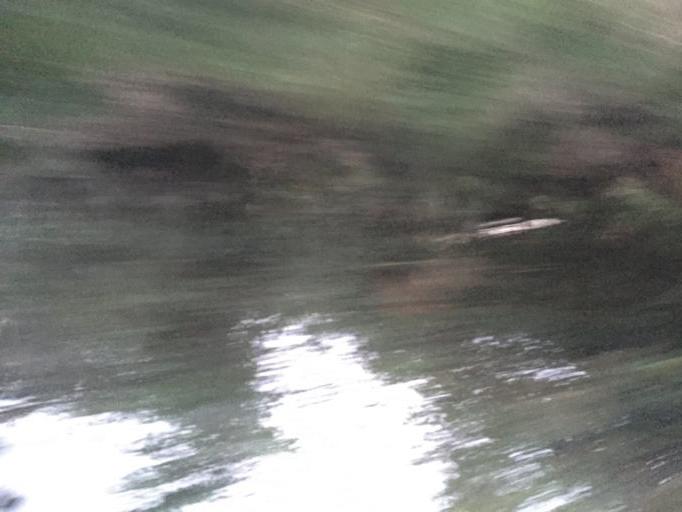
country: TW
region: Taiwan
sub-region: Yilan
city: Yilan
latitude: 24.7604
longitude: 121.7380
